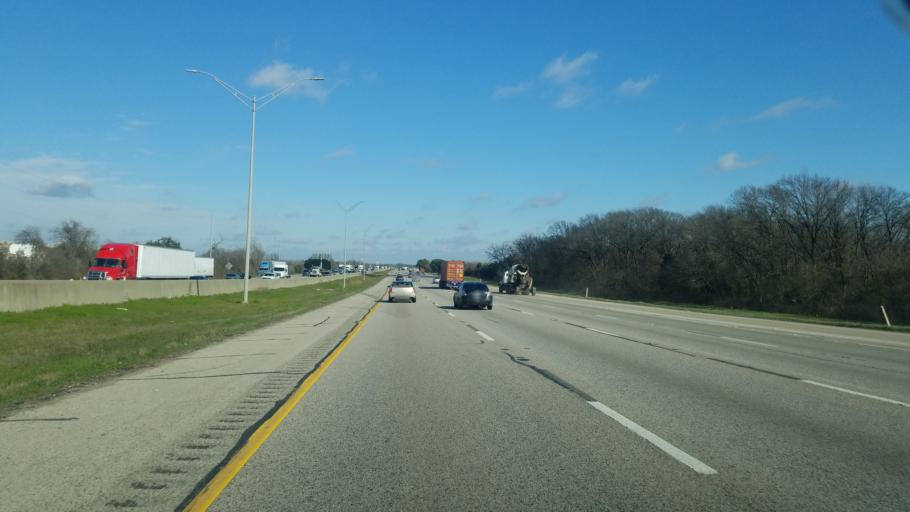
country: US
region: Texas
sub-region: Dallas County
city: Hutchins
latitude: 32.6665
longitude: -96.7173
